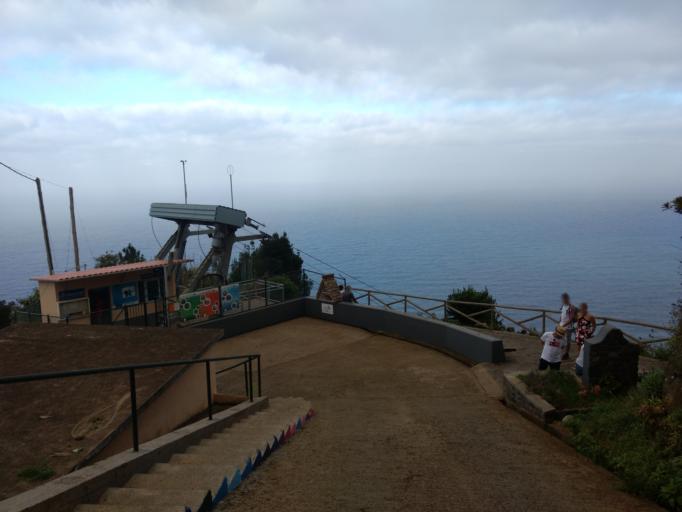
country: PT
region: Madeira
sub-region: Santana
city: Santana
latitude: 32.8146
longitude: -16.8767
